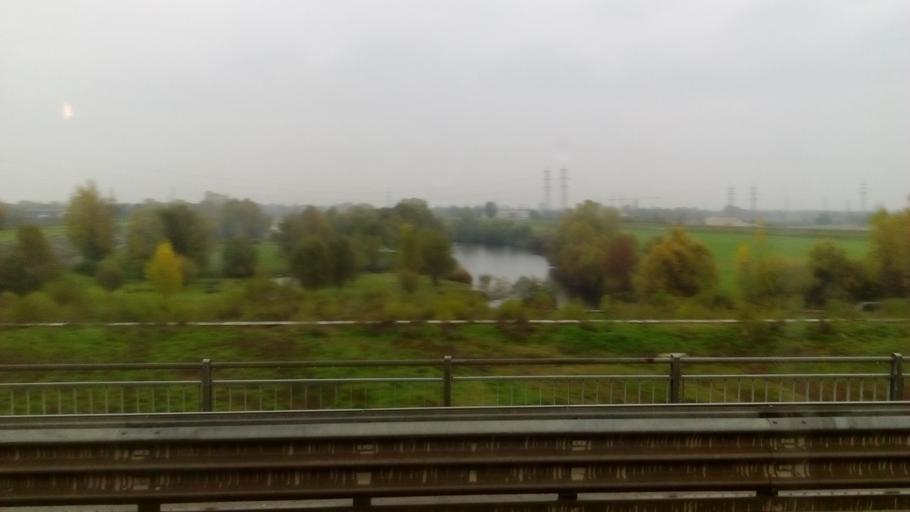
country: IT
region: Veneto
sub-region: Provincia di Vicenza
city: Sandrigo
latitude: 45.6507
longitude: 11.5802
